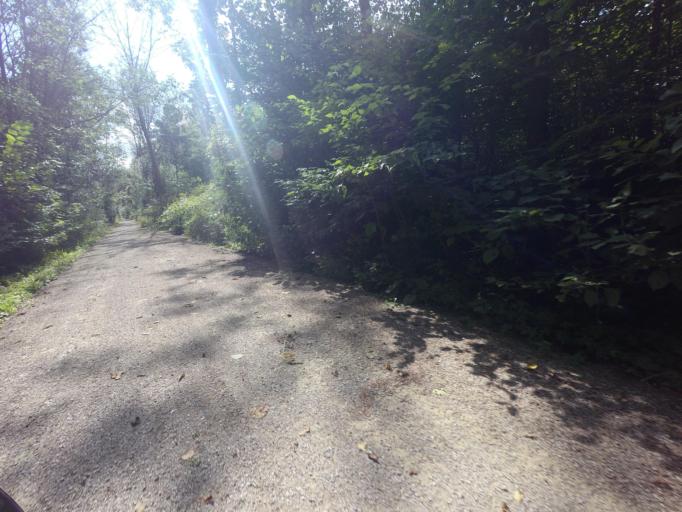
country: CA
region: Ontario
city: Huron East
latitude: 43.7057
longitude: -81.3613
